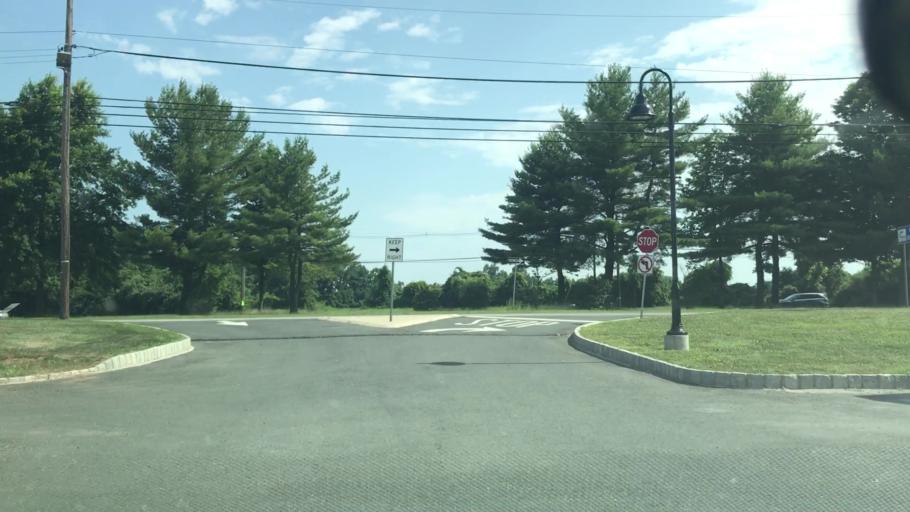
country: US
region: New Jersey
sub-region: Hunterdon County
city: Whitehouse Station
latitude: 40.6155
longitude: -74.7393
